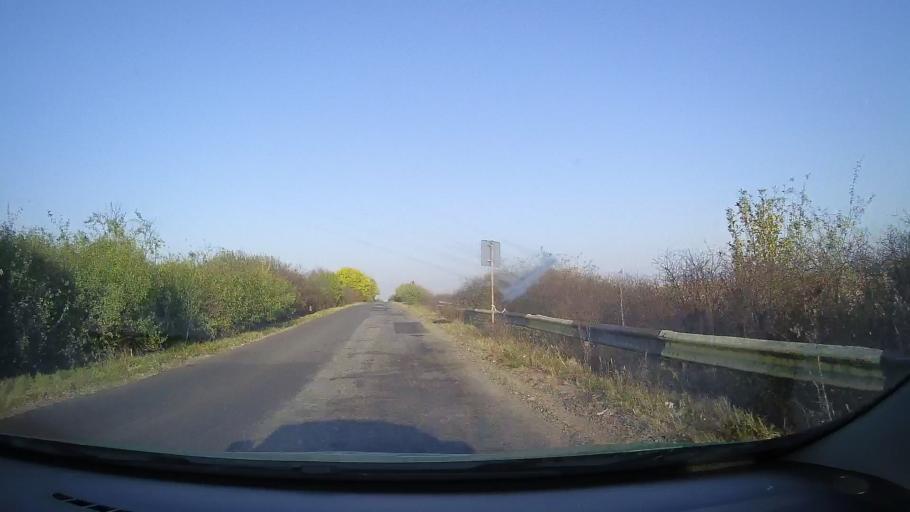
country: RO
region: Arad
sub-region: Comuna Tarnova
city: Agrisu Mare
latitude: 46.3110
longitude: 21.7498
